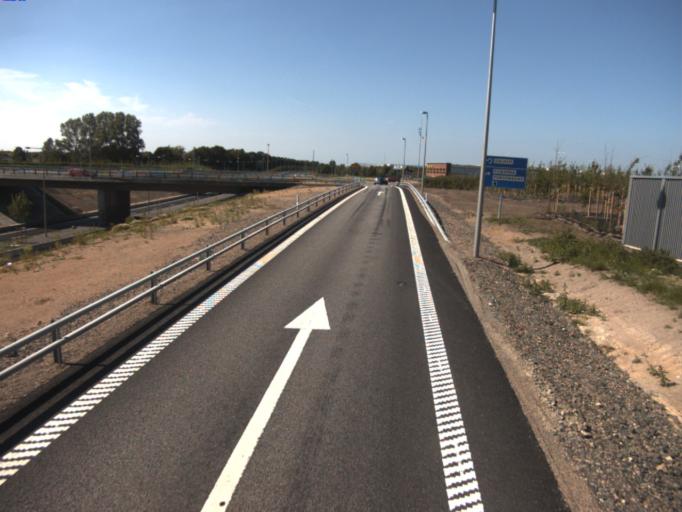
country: SE
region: Skane
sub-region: Helsingborg
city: Odakra
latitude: 56.0629
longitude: 12.7470
